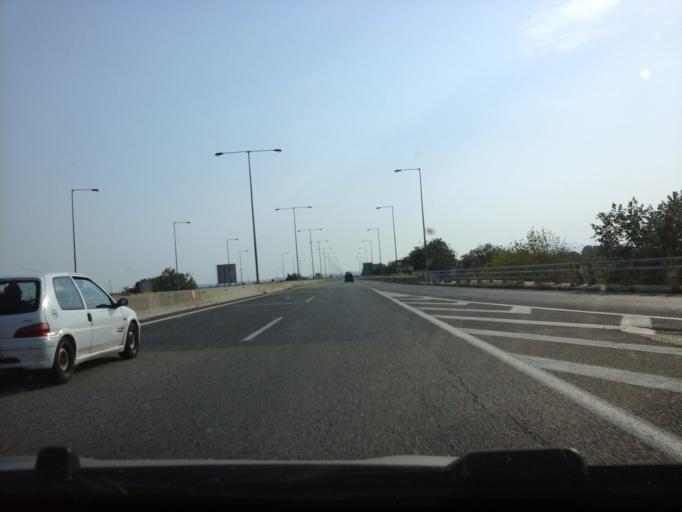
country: GR
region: East Macedonia and Thrace
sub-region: Nomos Xanthis
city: Genissea
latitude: 41.0973
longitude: 24.9457
